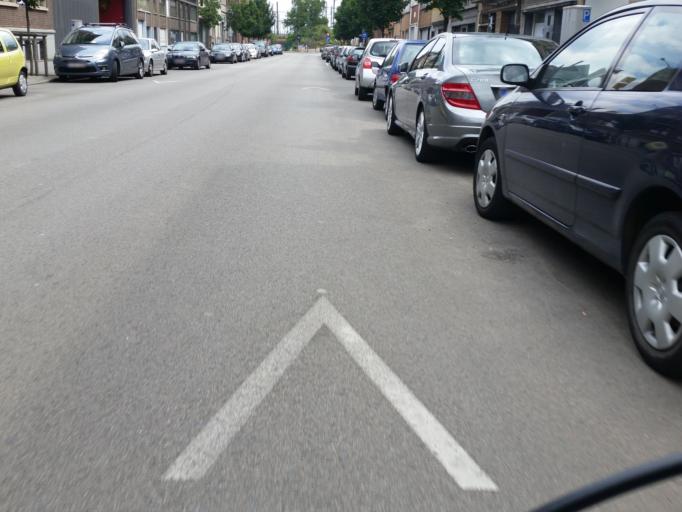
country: BE
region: Brussels Capital
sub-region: Bruxelles-Capitale
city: Brussels
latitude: 50.8694
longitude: 4.3633
